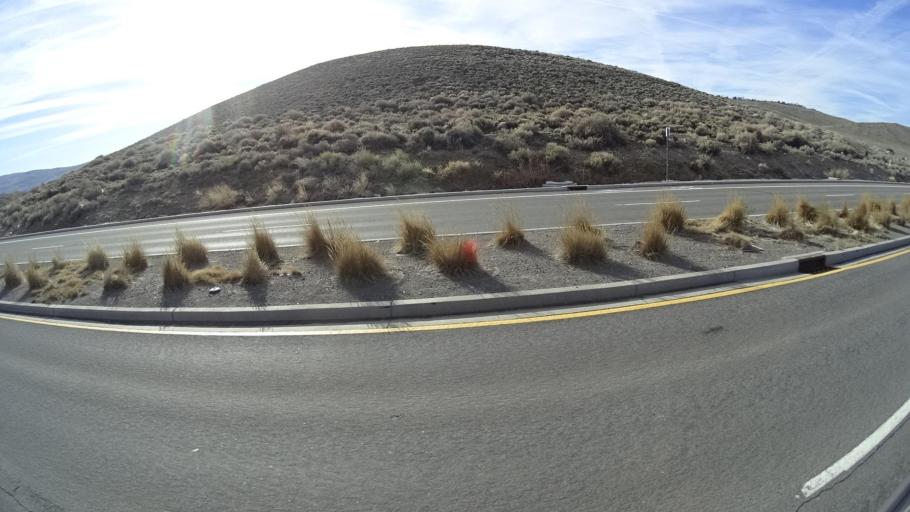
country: US
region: Nevada
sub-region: Washoe County
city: Spanish Springs
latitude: 39.6059
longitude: -119.7045
